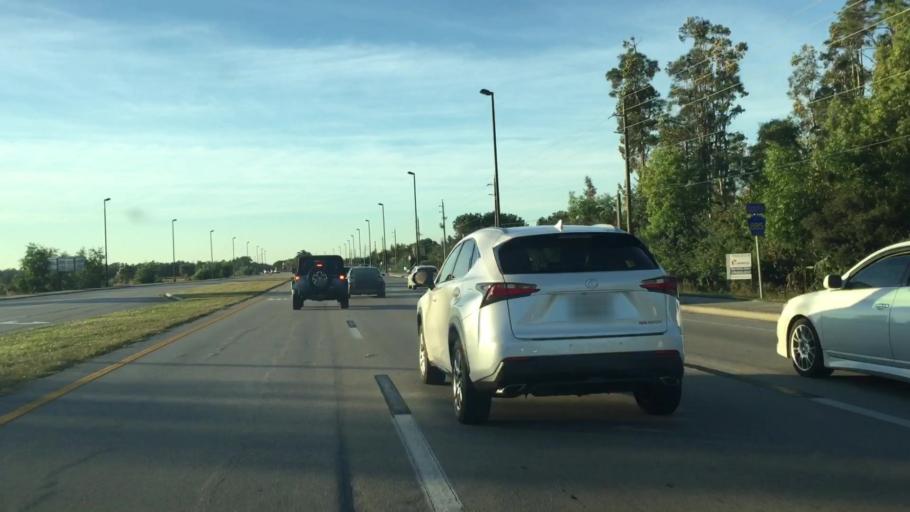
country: US
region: Florida
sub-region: Lee County
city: Gateway
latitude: 26.5444
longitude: -81.7864
